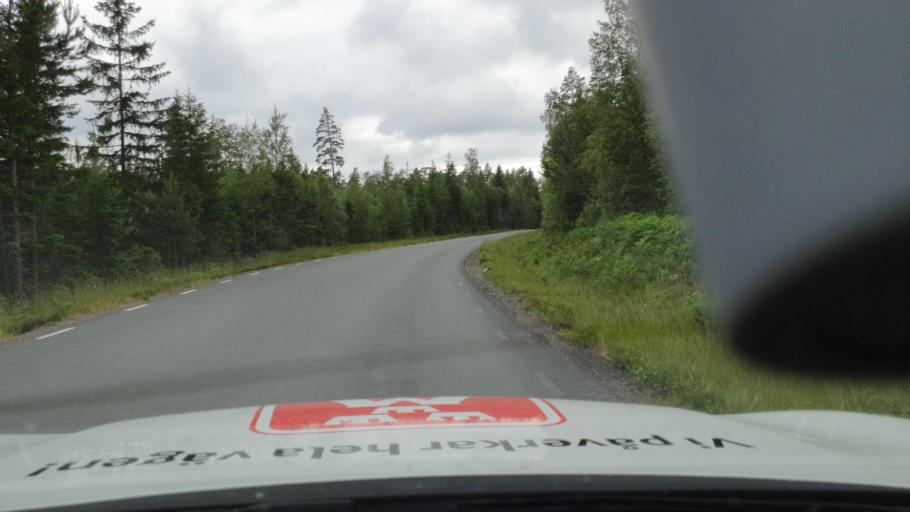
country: SE
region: Joenkoeping
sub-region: Habo Kommun
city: Habo
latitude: 58.1025
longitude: 14.1511
